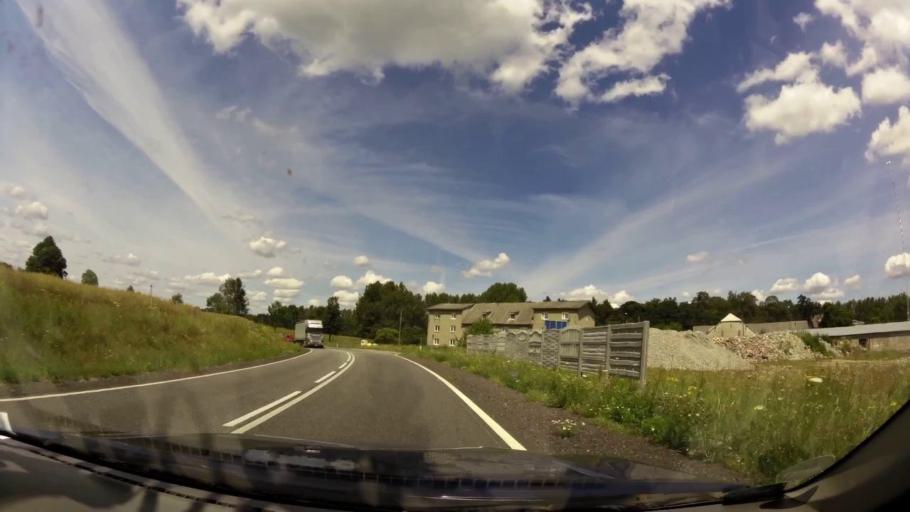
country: PL
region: West Pomeranian Voivodeship
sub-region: Powiat stargardzki
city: Insko
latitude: 53.4654
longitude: 15.5837
